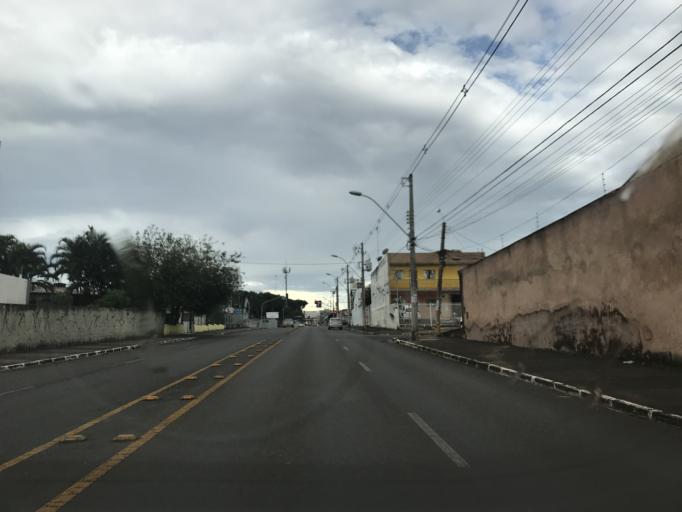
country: BR
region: Federal District
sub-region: Brasilia
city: Brasilia
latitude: -15.8445
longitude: -48.0513
